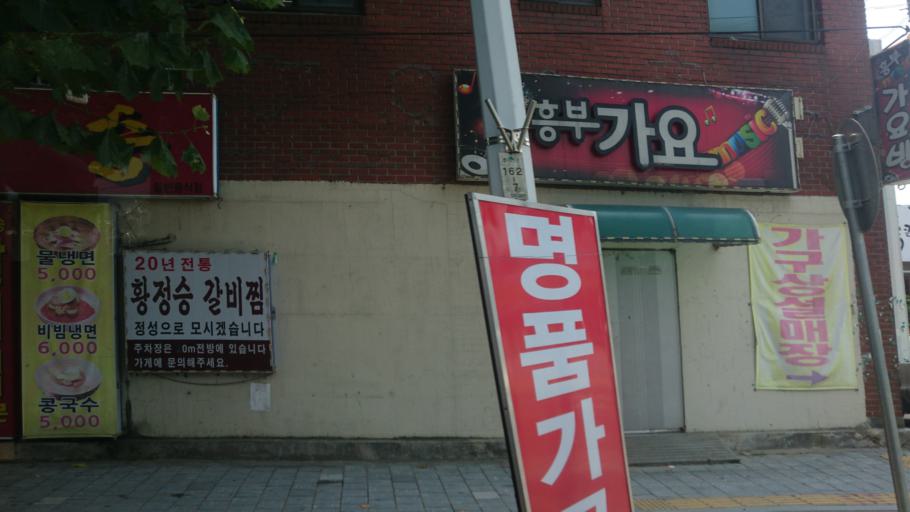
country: KR
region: Gyeongsangbuk-do
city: Gyeongsan-si
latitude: 35.8766
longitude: 128.6800
